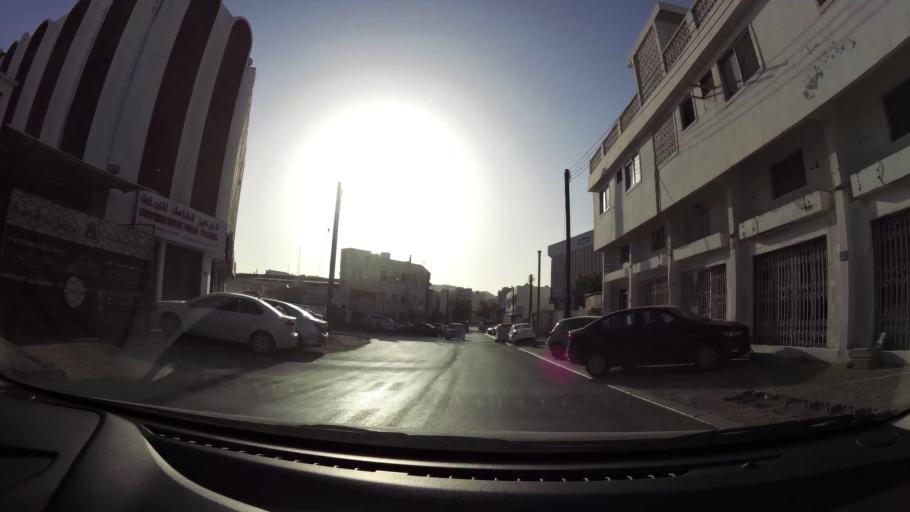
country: OM
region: Muhafazat Masqat
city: Muscat
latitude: 23.5896
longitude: 58.5569
